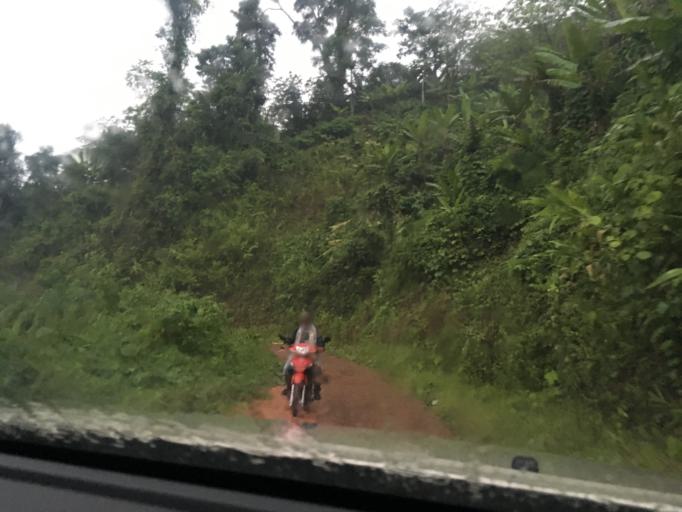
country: LA
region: Oudomxai
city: Muang La
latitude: 21.2459
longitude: 101.9405
